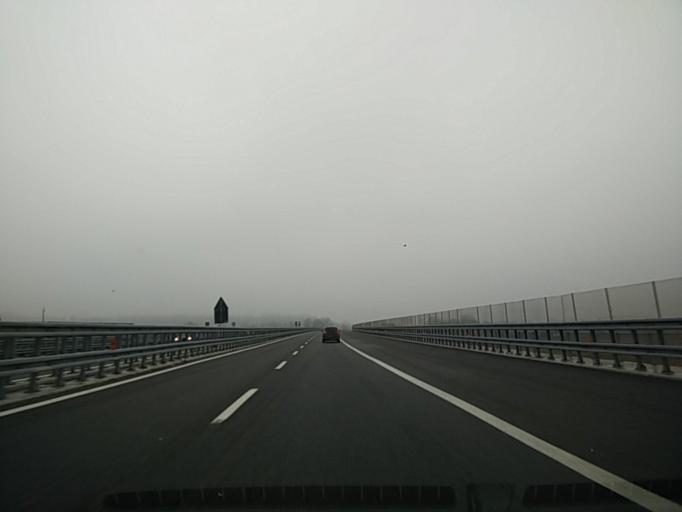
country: IT
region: Piedmont
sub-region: Provincia di Asti
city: Asti
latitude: 44.9142
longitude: 8.2244
